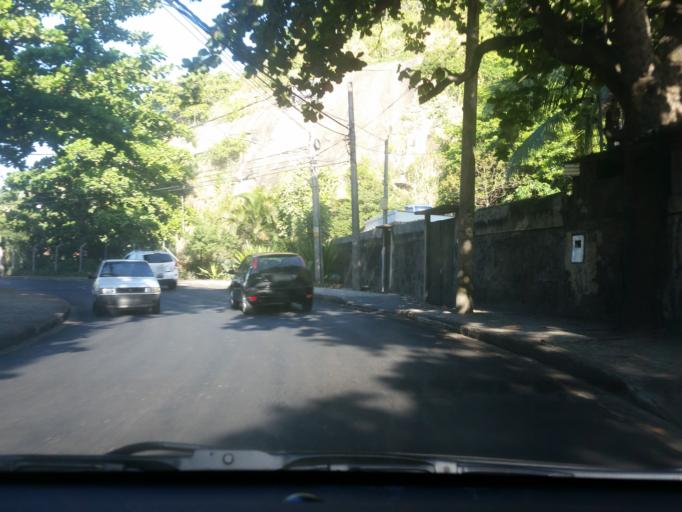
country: BR
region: Rio de Janeiro
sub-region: Nilopolis
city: Nilopolis
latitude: -23.0322
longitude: -43.4852
